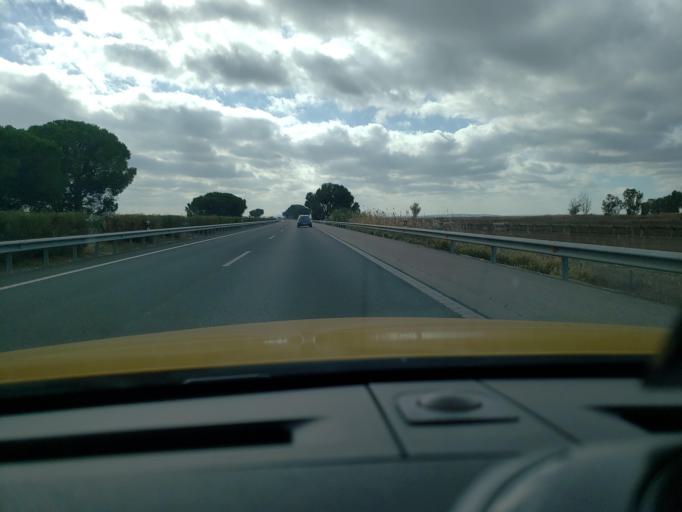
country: ES
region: Andalusia
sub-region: Provincia de Sevilla
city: Los Palacios y Villafranca
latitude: 37.0841
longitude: -5.9366
